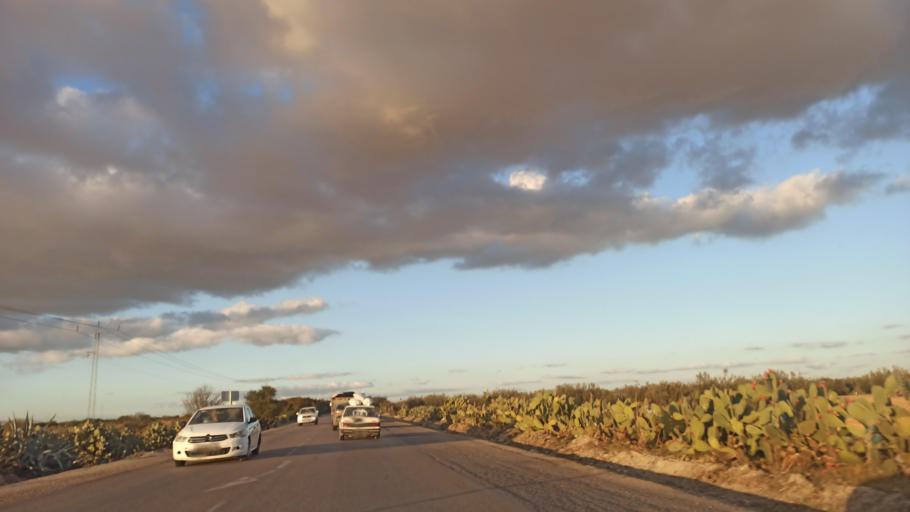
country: TN
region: Susah
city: Sidi Bou Ali
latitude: 36.0137
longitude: 10.3186
